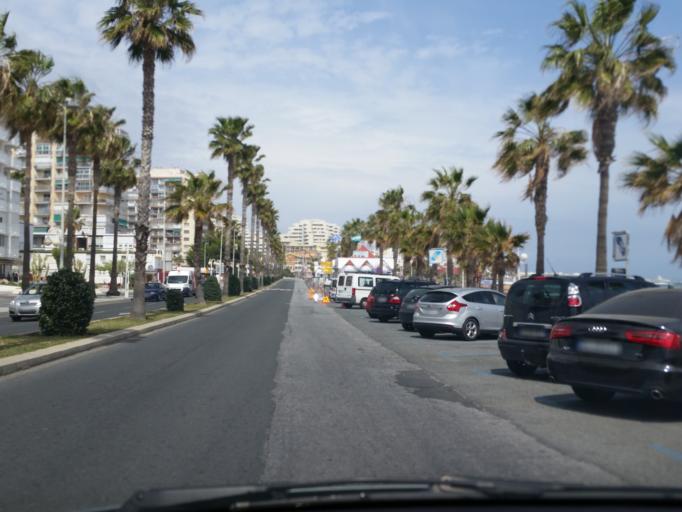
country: ES
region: Andalusia
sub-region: Provincia de Malaga
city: Benalmadena
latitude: 36.5857
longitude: -4.5332
